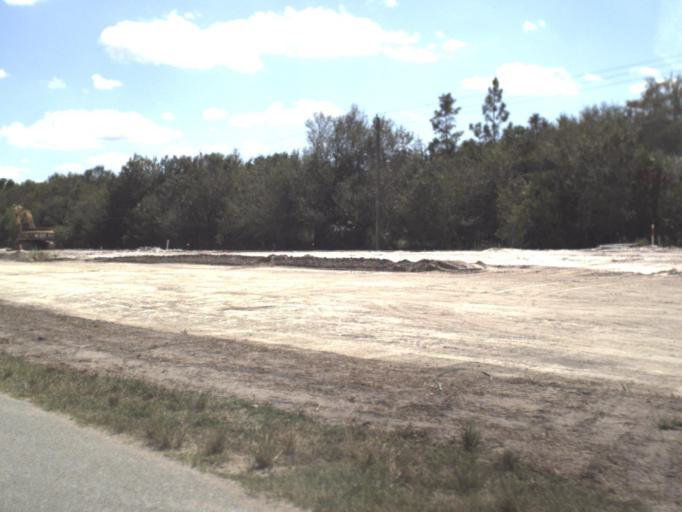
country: US
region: Florida
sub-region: Collier County
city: Lely Resort
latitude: 26.0528
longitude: -81.6827
